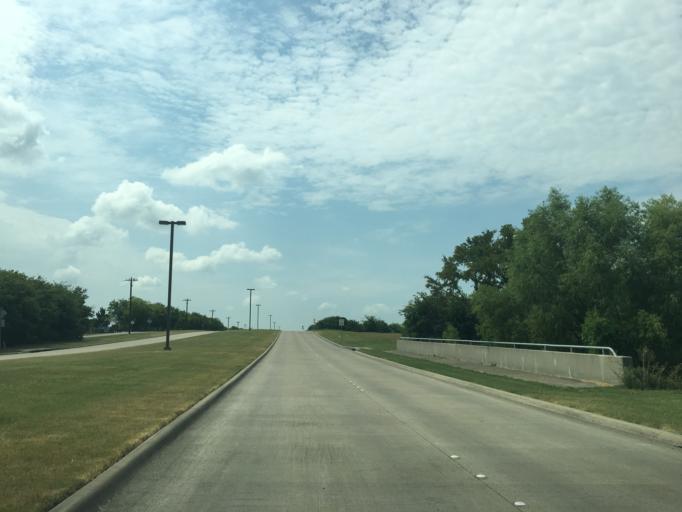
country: US
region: Texas
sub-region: Rockwall County
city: Rockwall
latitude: 32.9646
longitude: -96.4526
